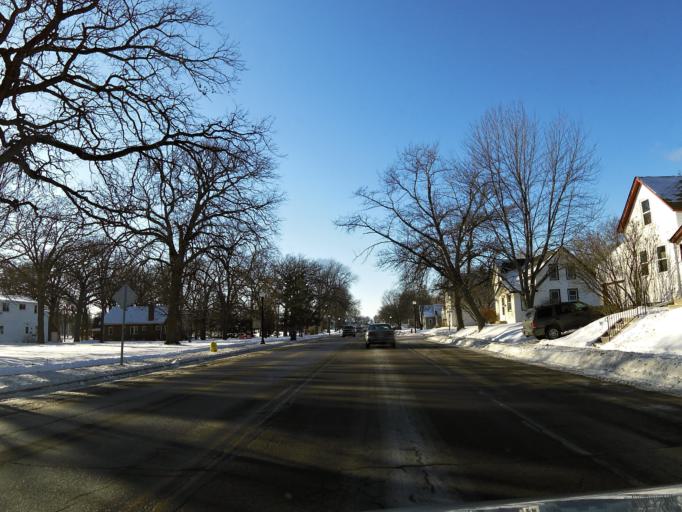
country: US
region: Minnesota
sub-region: Le Sueur County
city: New Prague
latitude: 44.5436
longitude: -93.5677
